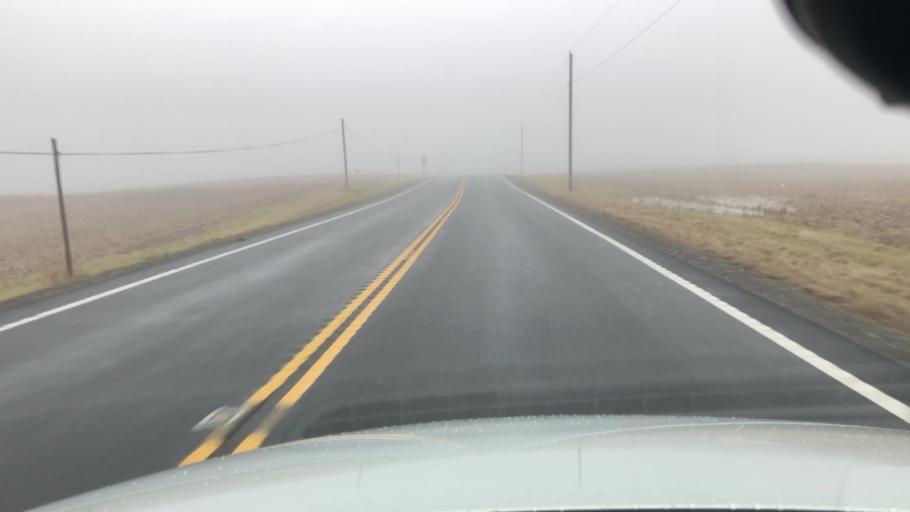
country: US
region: Ohio
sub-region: Logan County
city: Lakeview
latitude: 40.5946
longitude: -83.8655
